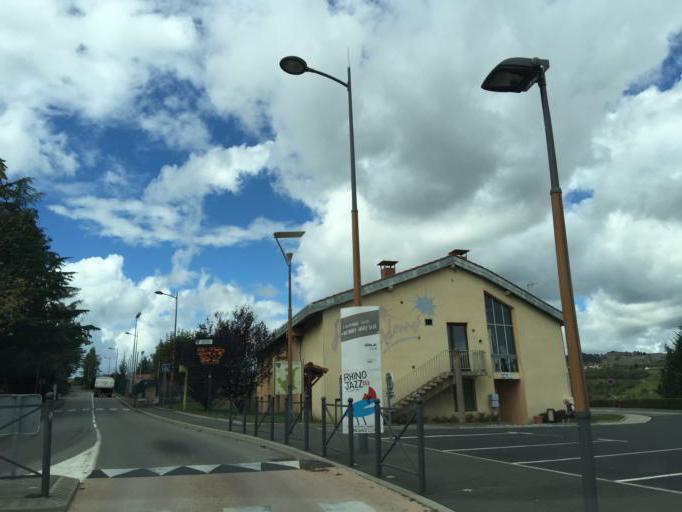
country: FR
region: Rhone-Alpes
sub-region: Departement de la Loire
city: Saint-Martin-la-Plaine
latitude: 45.5341
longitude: 4.5858
